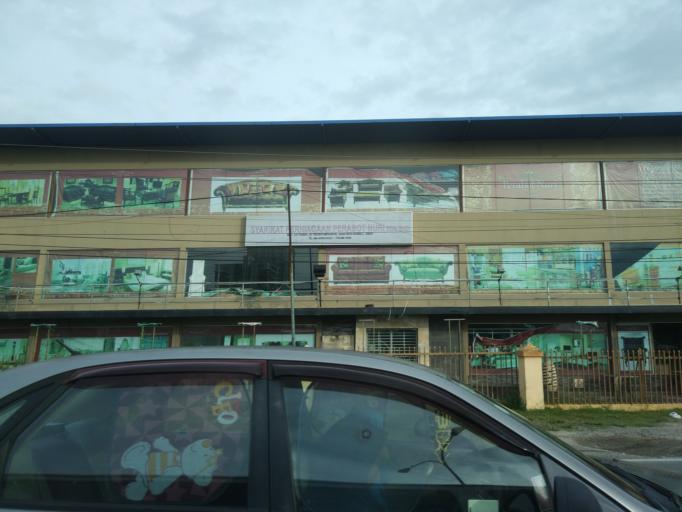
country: MY
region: Sabah
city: Kota Kinabalu
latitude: 6.0478
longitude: 116.1647
